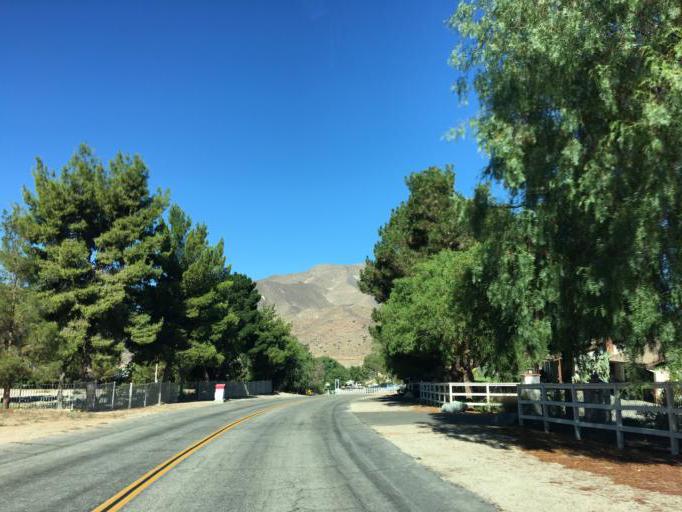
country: US
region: California
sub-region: Los Angeles County
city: Acton
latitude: 34.4575
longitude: -118.1883
